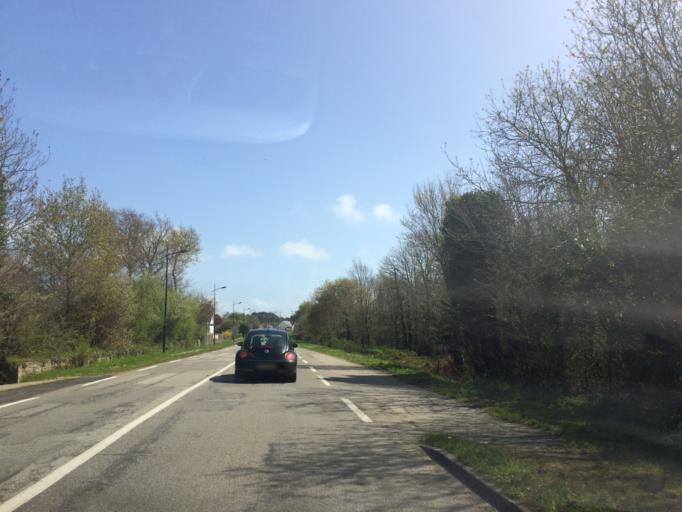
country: FR
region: Brittany
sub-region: Departement du Morbihan
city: La Trinite-sur-Mer
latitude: 47.5968
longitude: -3.0391
